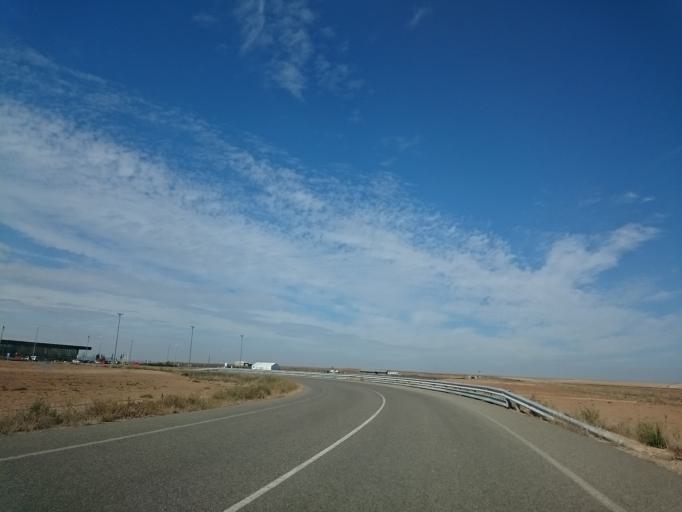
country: ES
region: Catalonia
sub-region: Provincia de Lleida
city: Alguaire
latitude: 41.7290
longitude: 0.5463
